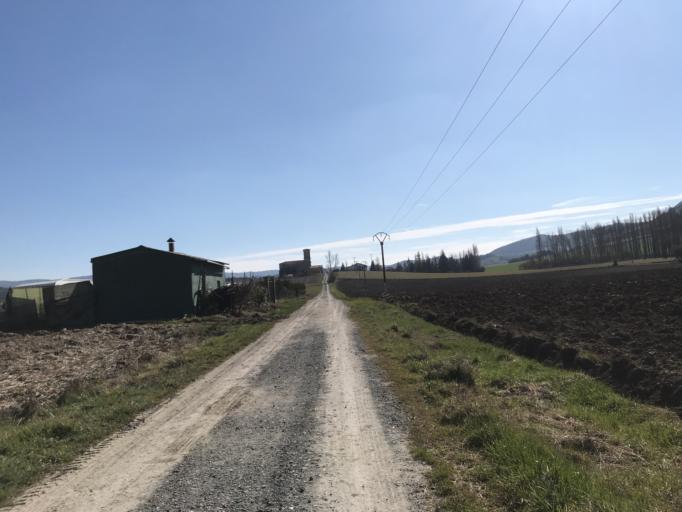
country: ES
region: Basque Country
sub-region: Provincia de Alava
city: Gasteiz / Vitoria
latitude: 42.8241
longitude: -2.6535
